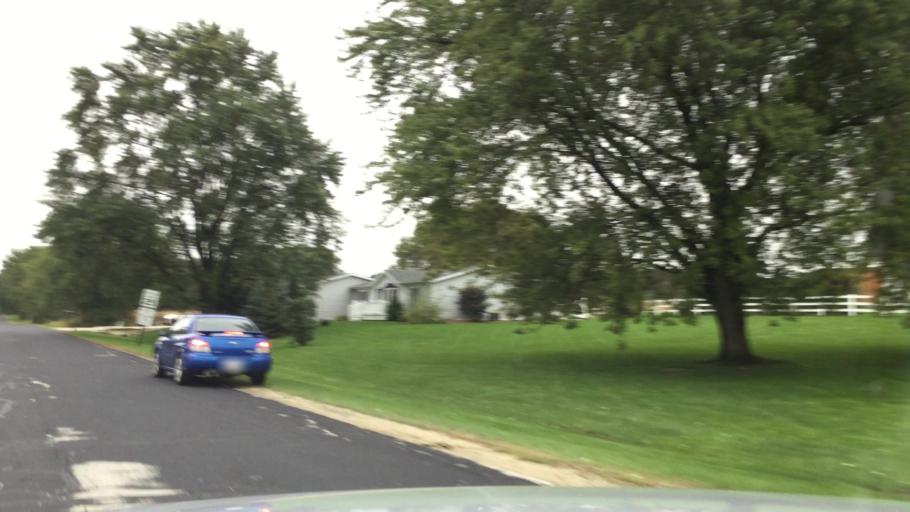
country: US
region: Wisconsin
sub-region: Racine County
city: Waterford
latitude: 42.7637
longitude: -88.1848
